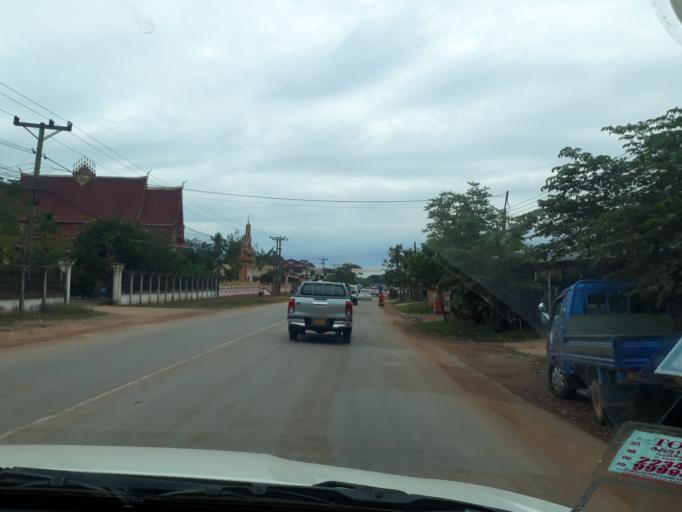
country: LA
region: Vientiane
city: Muang Phon-Hong
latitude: 18.3417
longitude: 102.4318
